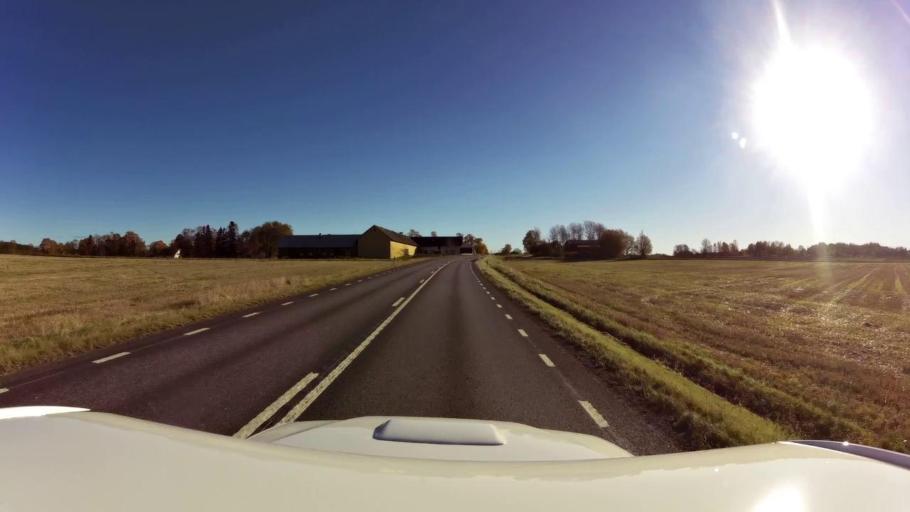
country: SE
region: OEstergoetland
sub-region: Linkopings Kommun
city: Ljungsbro
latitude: 58.5292
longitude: 15.4053
